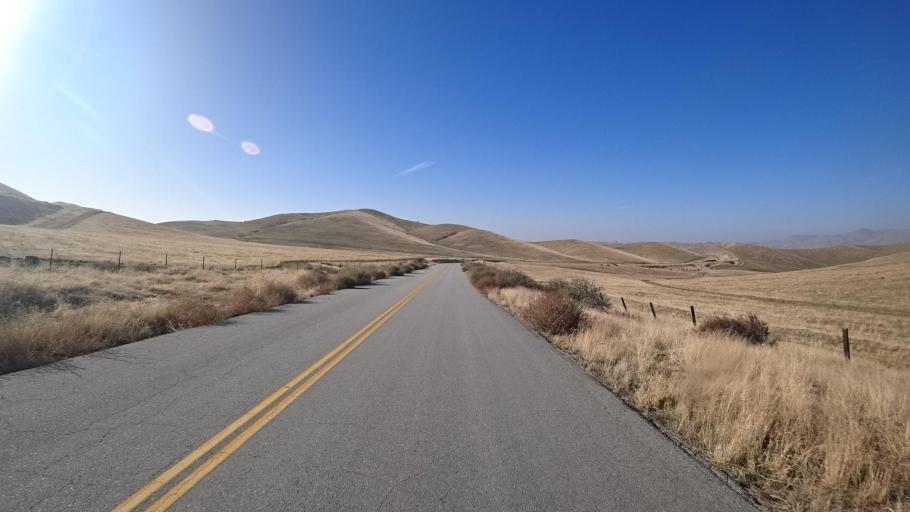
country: US
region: California
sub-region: Kern County
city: Bear Valley Springs
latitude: 35.2718
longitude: -118.6855
